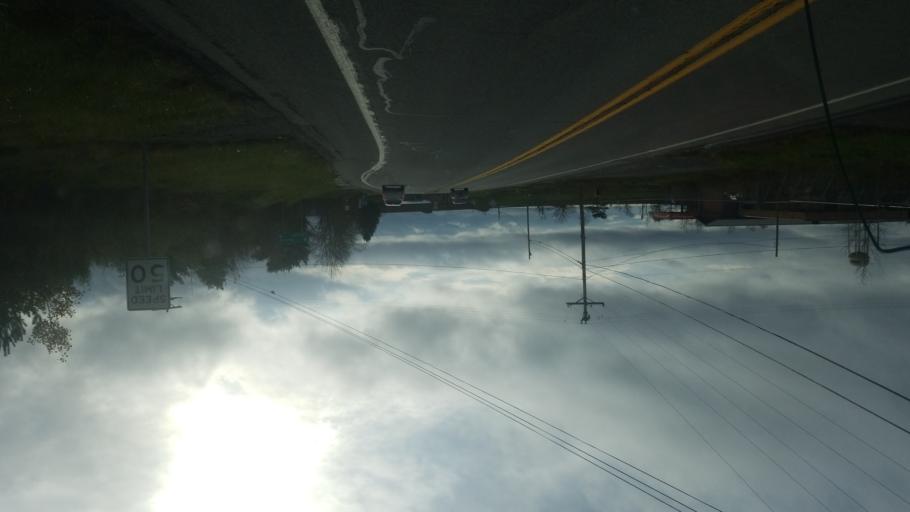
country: US
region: Pennsylvania
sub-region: Jefferson County
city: Brookville
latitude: 41.1706
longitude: -79.0440
